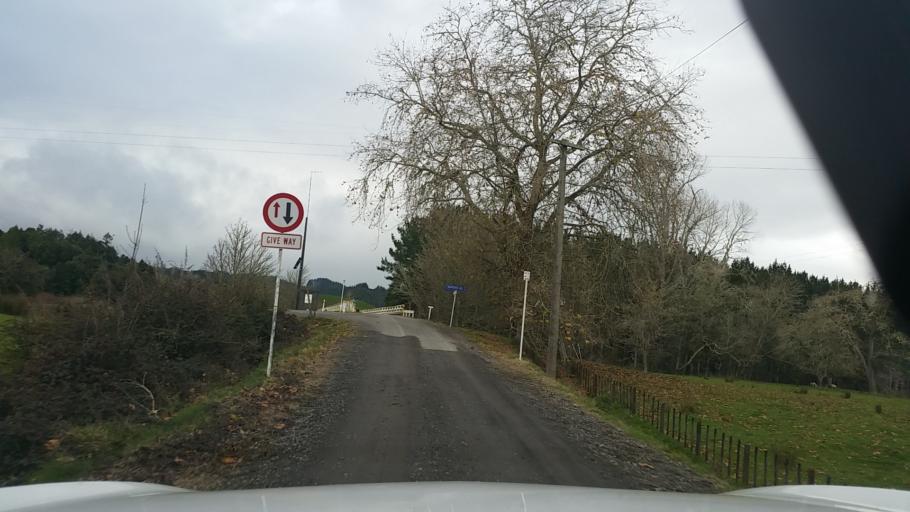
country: NZ
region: Taranaki
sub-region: New Plymouth District
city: Waitara
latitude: -39.1525
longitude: 174.5209
